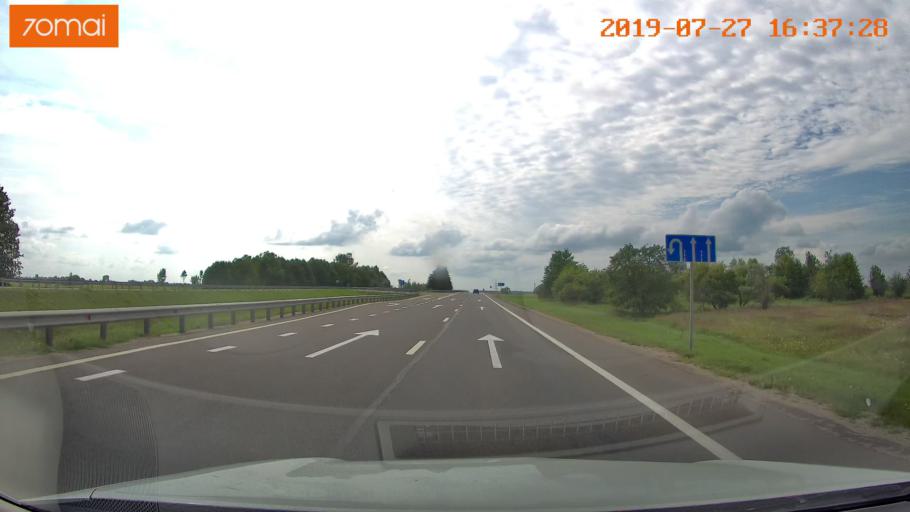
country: RU
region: Kaliningrad
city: Gvardeysk
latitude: 54.6483
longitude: 21.2550
